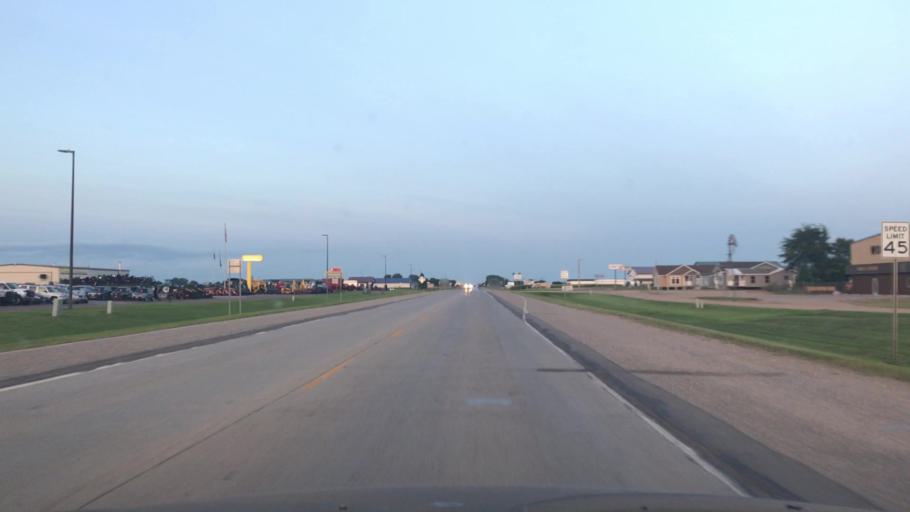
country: US
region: Minnesota
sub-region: Redwood County
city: Redwood Falls
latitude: 44.5414
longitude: -95.0855
